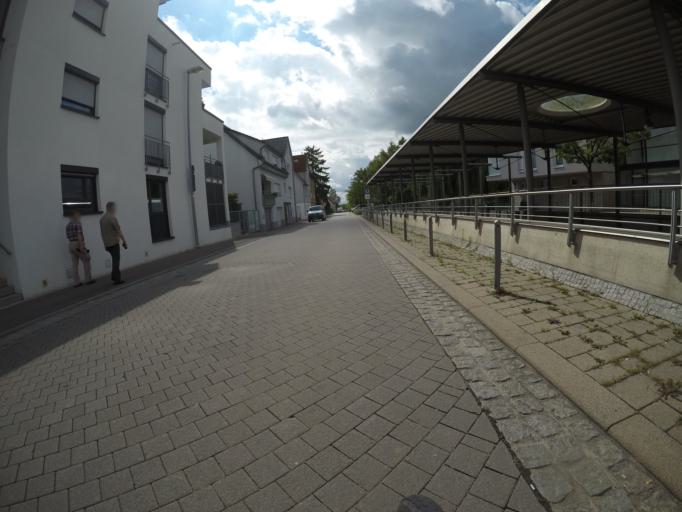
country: DE
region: Baden-Wuerttemberg
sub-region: Regierungsbezirk Stuttgart
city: Ostfildern
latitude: 48.7310
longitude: 9.2538
